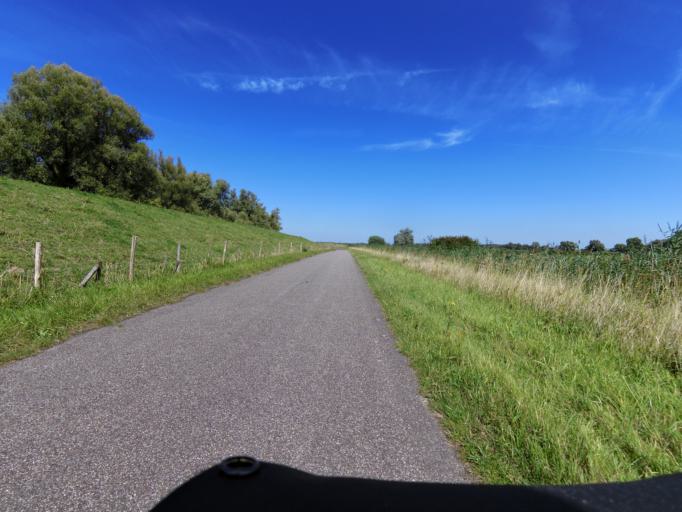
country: NL
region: South Holland
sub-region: Gemeente Sliedrecht
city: Sliedrecht
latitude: 51.7598
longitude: 4.7536
